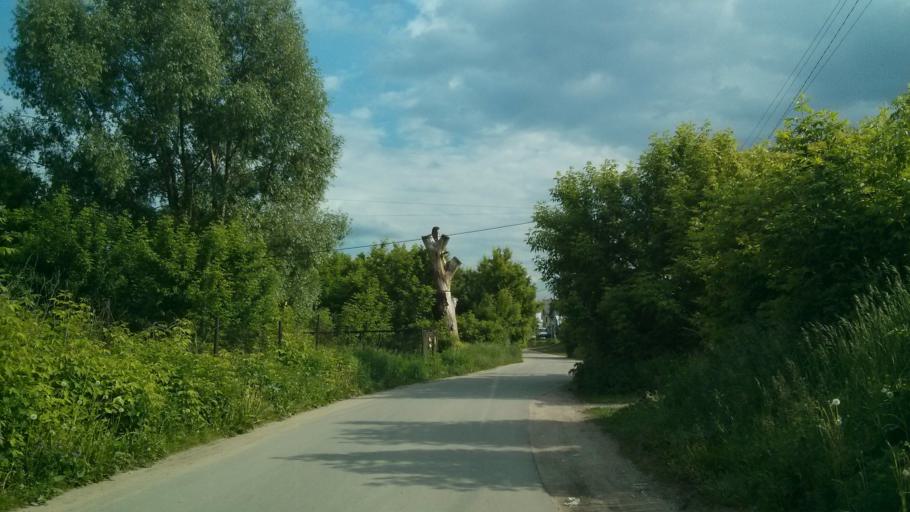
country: RU
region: Nizjnij Novgorod
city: Afonino
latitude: 56.2768
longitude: 44.1037
